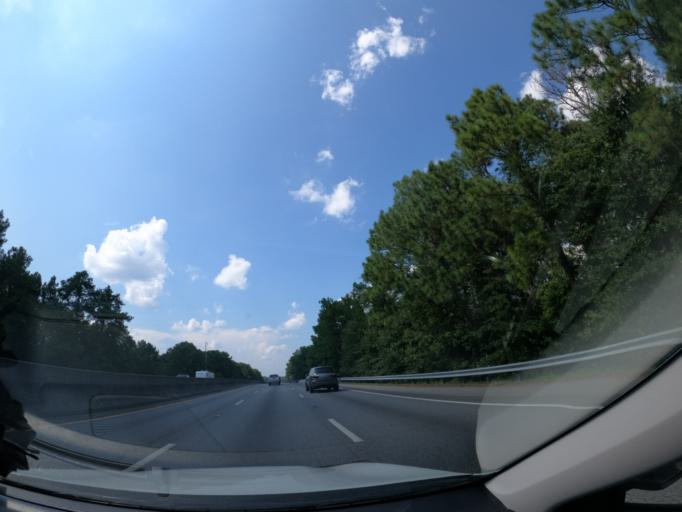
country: US
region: South Carolina
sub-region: Lexington County
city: Springdale
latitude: 33.9453
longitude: -81.0894
